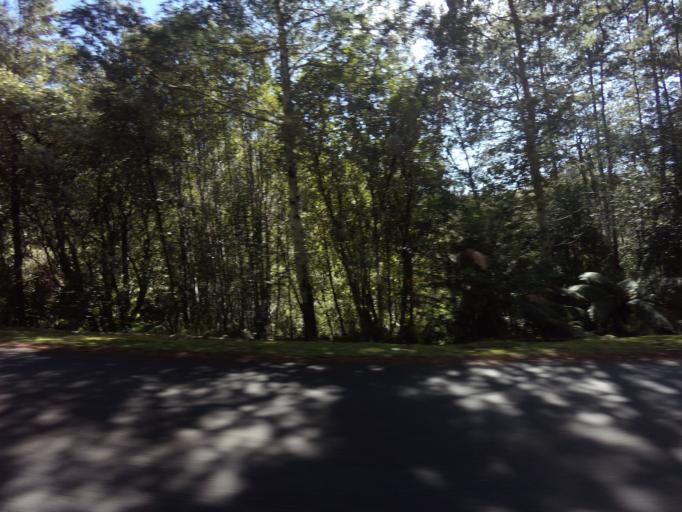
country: AU
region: Tasmania
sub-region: Derwent Valley
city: New Norfolk
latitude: -42.7471
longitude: 146.5015
